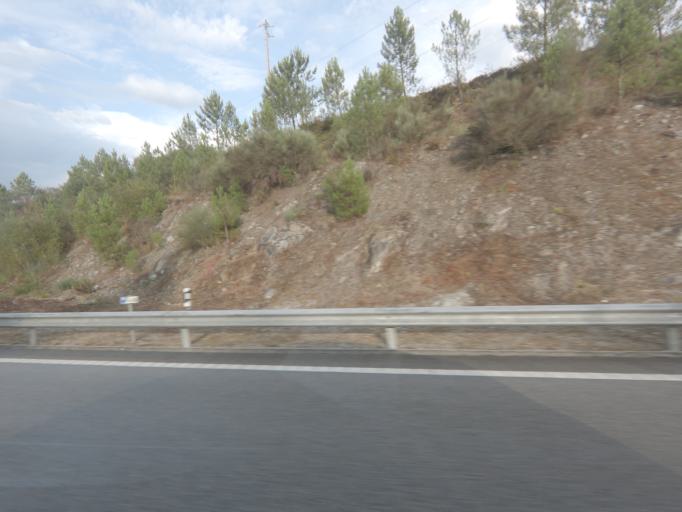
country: PT
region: Viseu
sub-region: Castro Daire
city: Castro Daire
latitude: 40.8195
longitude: -7.9396
